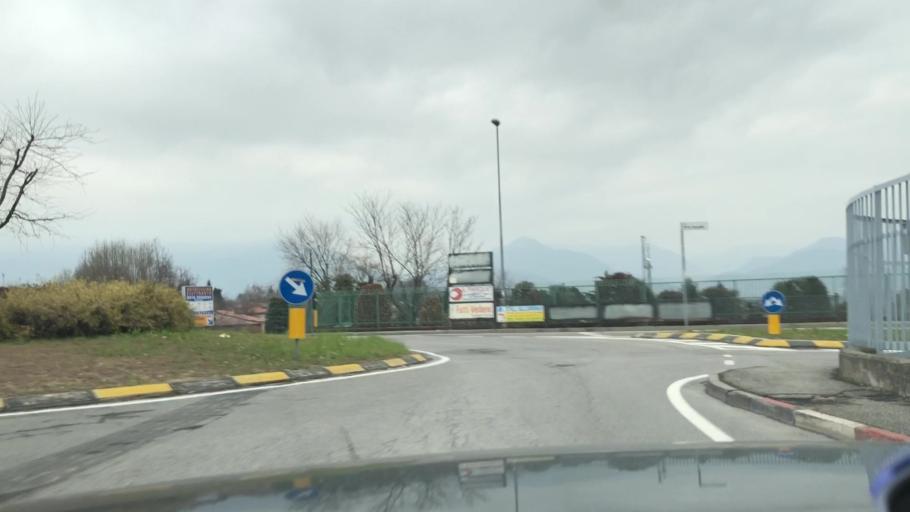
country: IT
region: Lombardy
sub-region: Provincia di Bergamo
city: Ponte San Pietro
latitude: 45.7081
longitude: 9.5838
